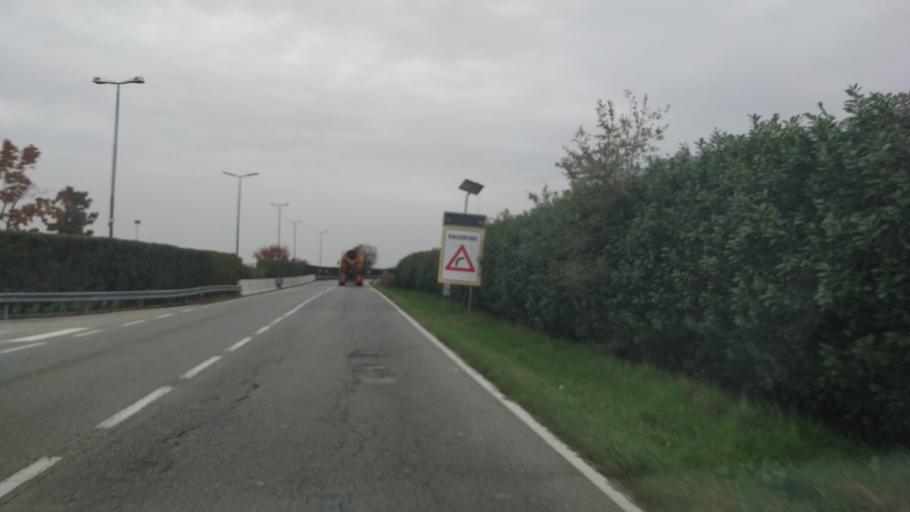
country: IT
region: Piedmont
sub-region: Provincia di Novara
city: Casalino
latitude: 45.3933
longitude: 8.5107
